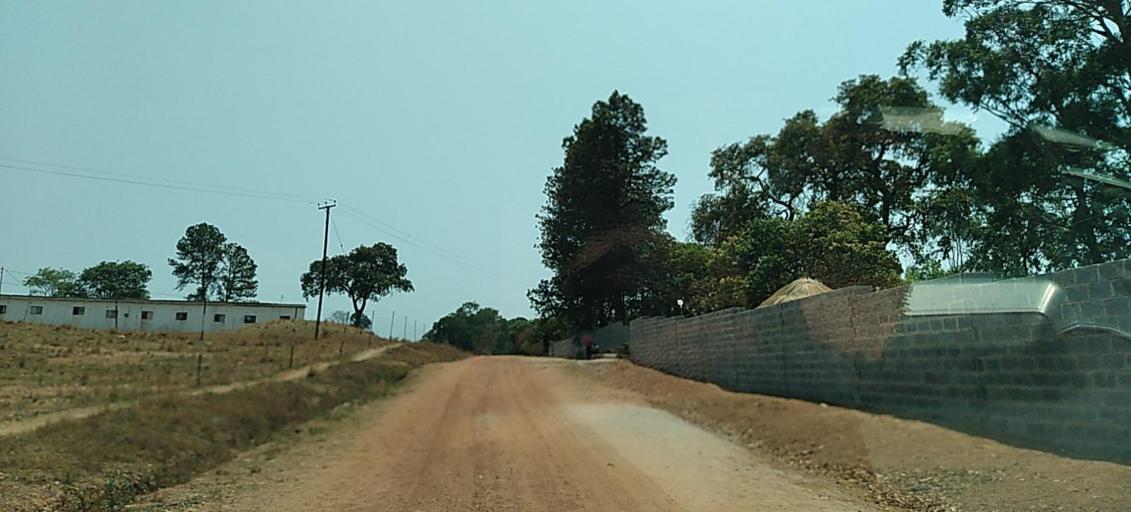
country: ZM
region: Copperbelt
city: Chingola
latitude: -12.6253
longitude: 27.9409
